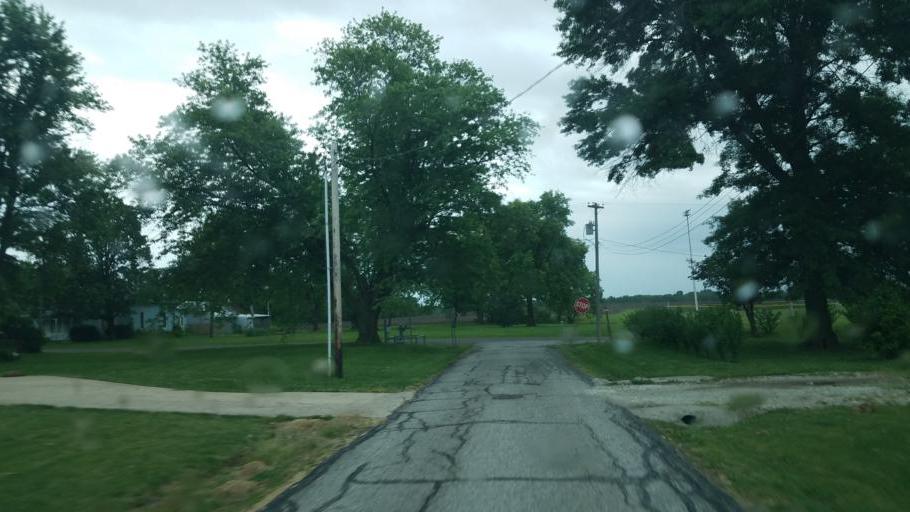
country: US
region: Missouri
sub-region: Moniteau County
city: California
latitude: 38.8117
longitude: -92.5915
